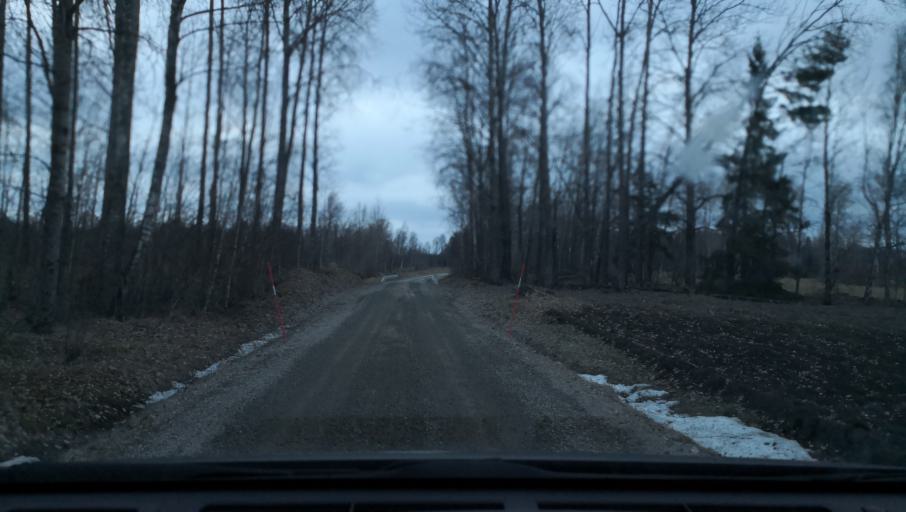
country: SE
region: OErebro
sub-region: Lindesbergs Kommun
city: Fellingsbro
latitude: 59.6051
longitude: 15.6116
